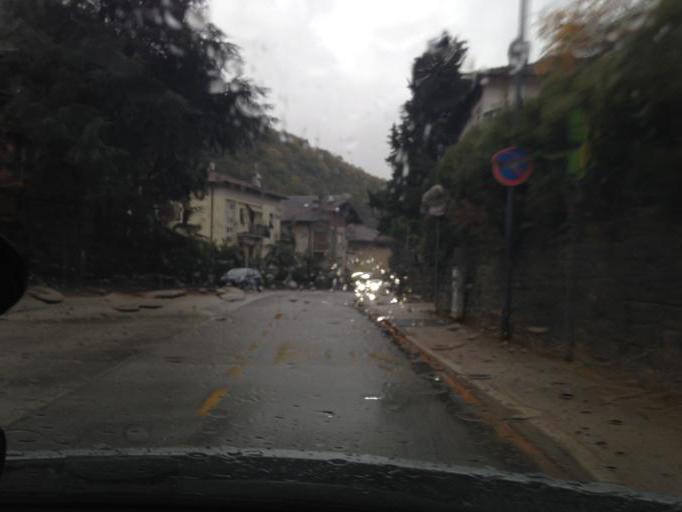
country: IT
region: Trentino-Alto Adige
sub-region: Provincia di Trento
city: Villa Lagarina
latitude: 45.9015
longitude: 11.0462
